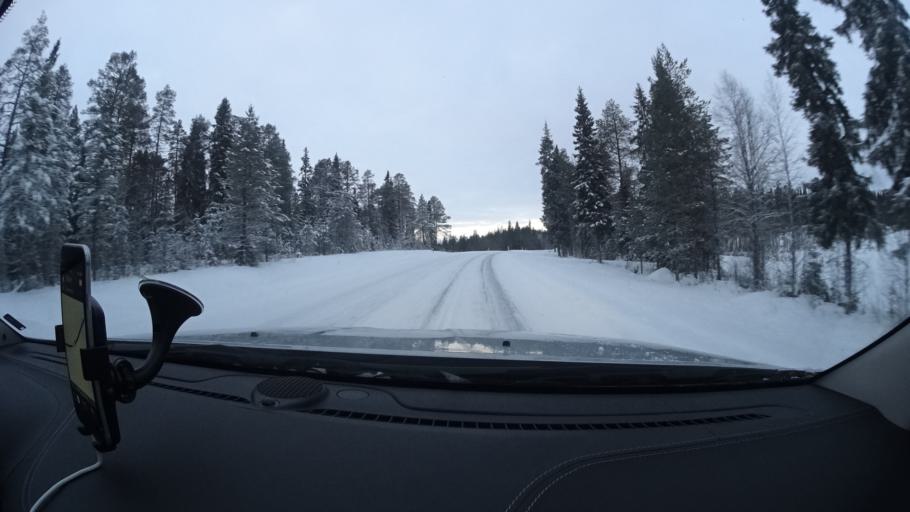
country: FI
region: Lapland
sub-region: Itae-Lappi
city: Posio
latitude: 66.0933
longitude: 28.6641
